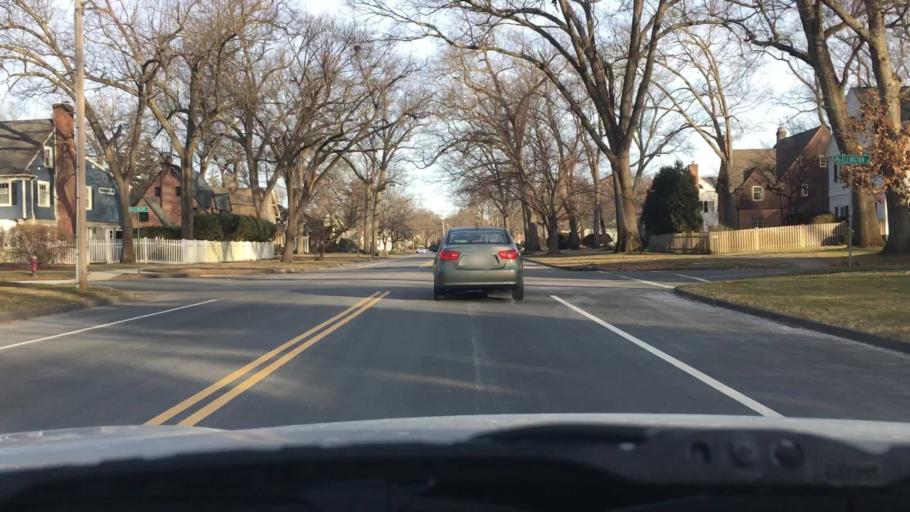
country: US
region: Massachusetts
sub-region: Hampden County
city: Longmeadow
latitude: 42.0629
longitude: -72.5734
